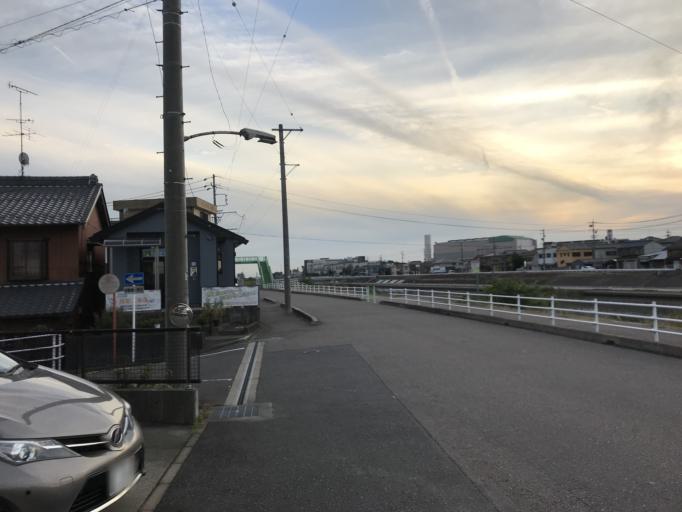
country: JP
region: Aichi
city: Nagoya-shi
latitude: 35.1941
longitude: 136.8507
